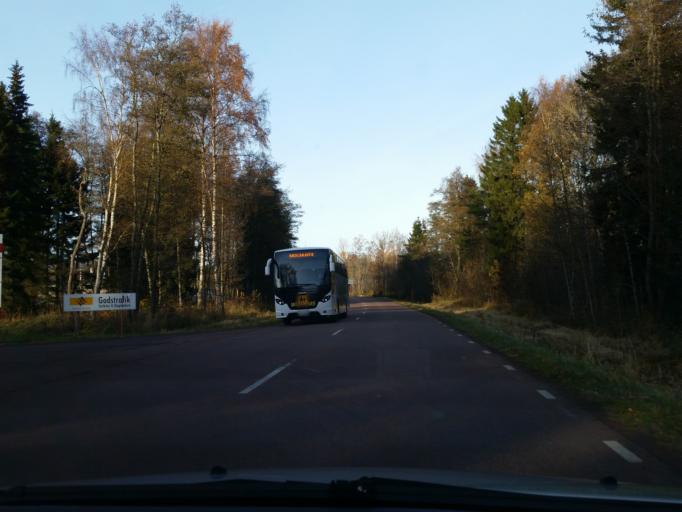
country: AX
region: Mariehamns stad
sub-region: Mariehamn
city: Mariehamn
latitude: 60.1193
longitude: 19.9162
